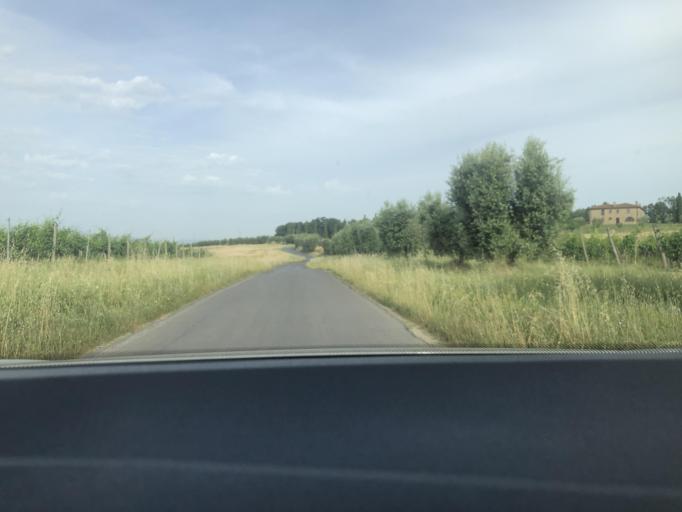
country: IT
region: Tuscany
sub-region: Provincia di Pistoia
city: Lamporecchio
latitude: 43.8118
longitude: 10.8786
